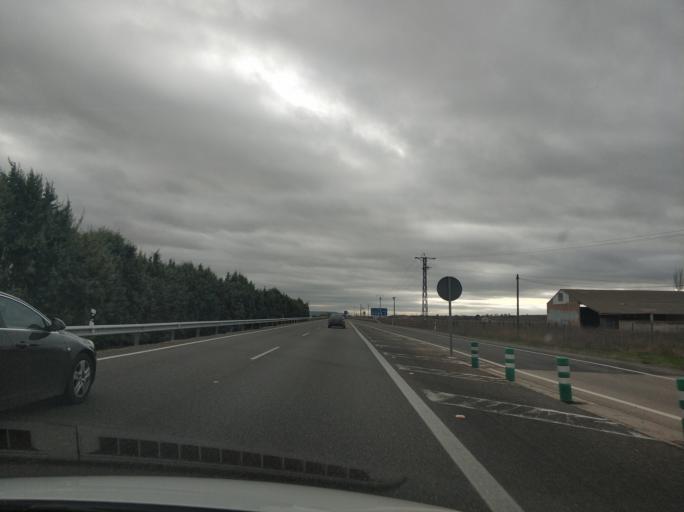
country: ES
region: Castille and Leon
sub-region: Provincia de Palencia
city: Duenas
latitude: 41.8508
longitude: -4.5576
